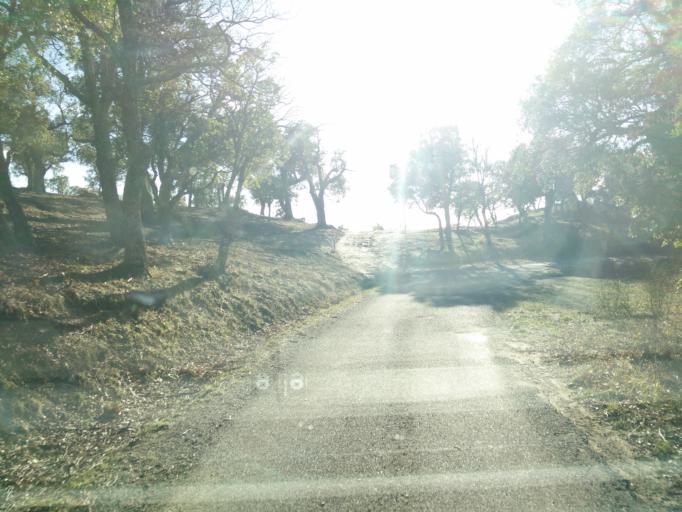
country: FR
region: Provence-Alpes-Cote d'Azur
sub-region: Departement du Var
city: Collobrieres
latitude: 43.2713
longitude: 6.3009
